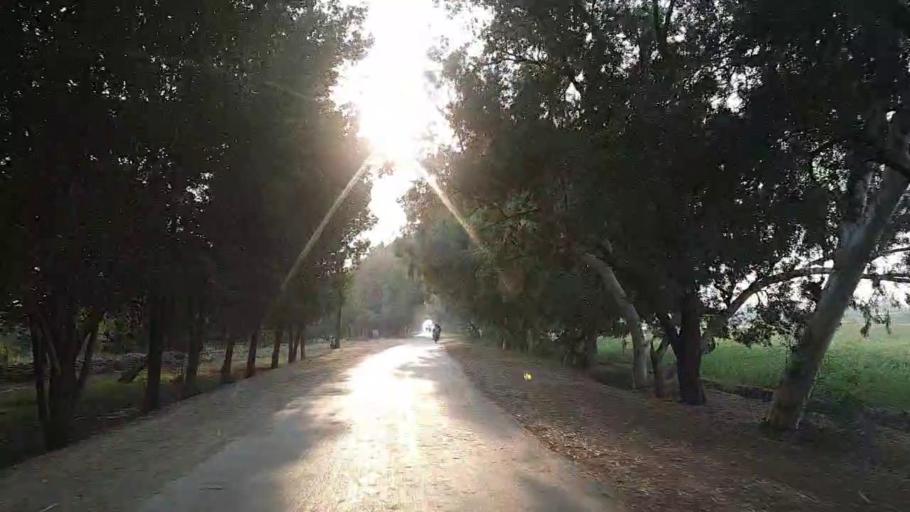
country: PK
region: Sindh
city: Mirwah Gorchani
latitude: 25.3093
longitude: 69.2139
